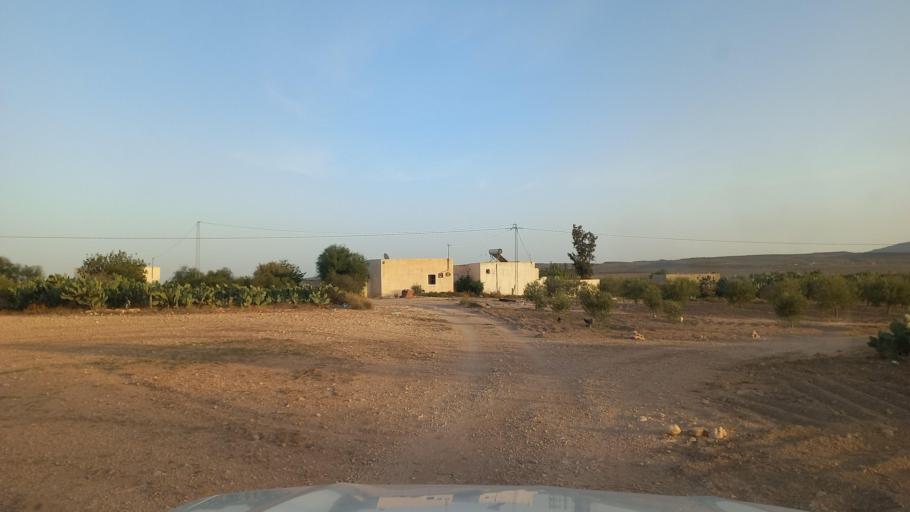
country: TN
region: Al Qasrayn
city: Kasserine
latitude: 35.2402
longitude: 8.9889
